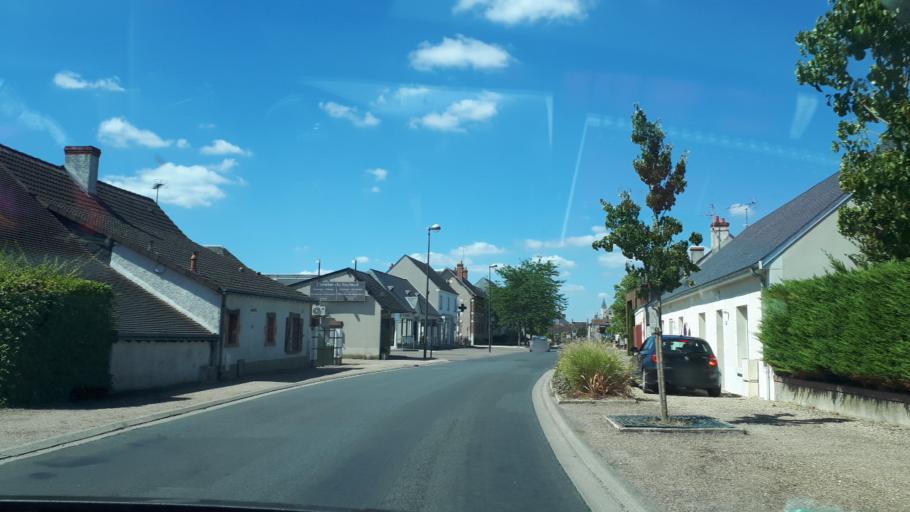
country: FR
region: Centre
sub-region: Departement du Loir-et-Cher
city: Mont-pres-Chambord
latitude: 47.5625
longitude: 1.4574
